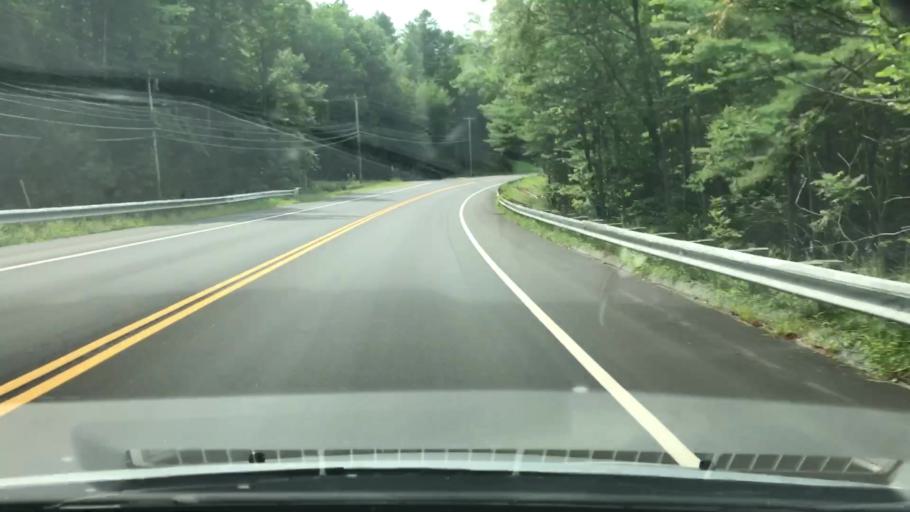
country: US
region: New Hampshire
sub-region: Grafton County
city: Lyme
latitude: 43.7505
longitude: -72.2138
